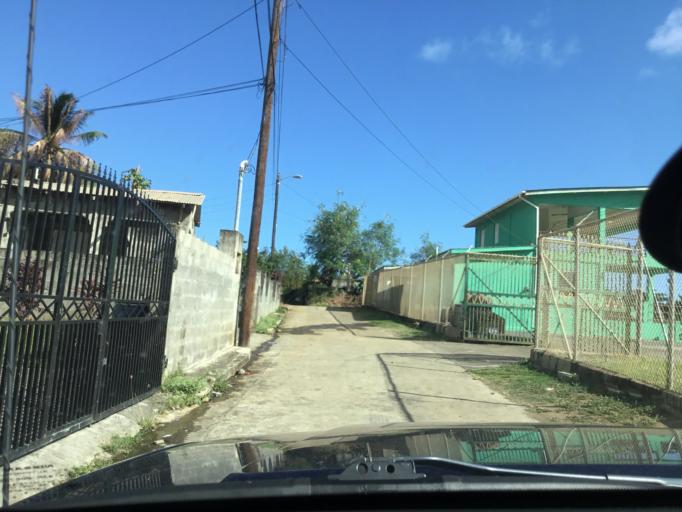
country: VC
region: Charlotte
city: Biabou
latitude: 13.1476
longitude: -61.1578
